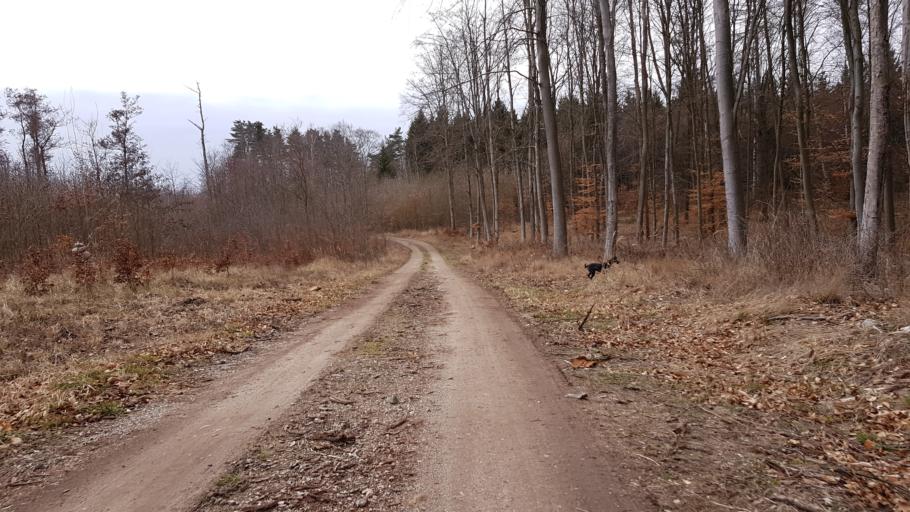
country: PL
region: West Pomeranian Voivodeship
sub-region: Powiat pyrzycki
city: Kozielice
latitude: 53.0842
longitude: 14.7478
